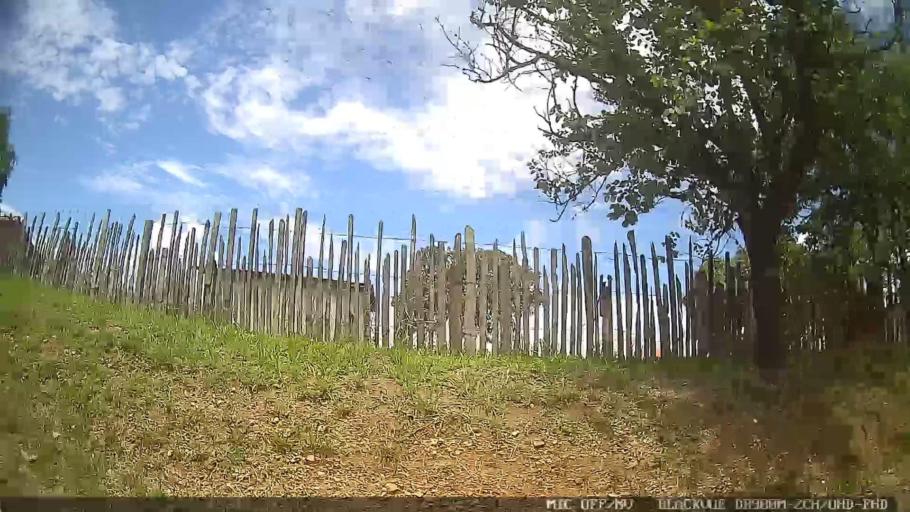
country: BR
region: Sao Paulo
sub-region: Conchas
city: Conchas
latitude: -23.0800
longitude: -47.9759
